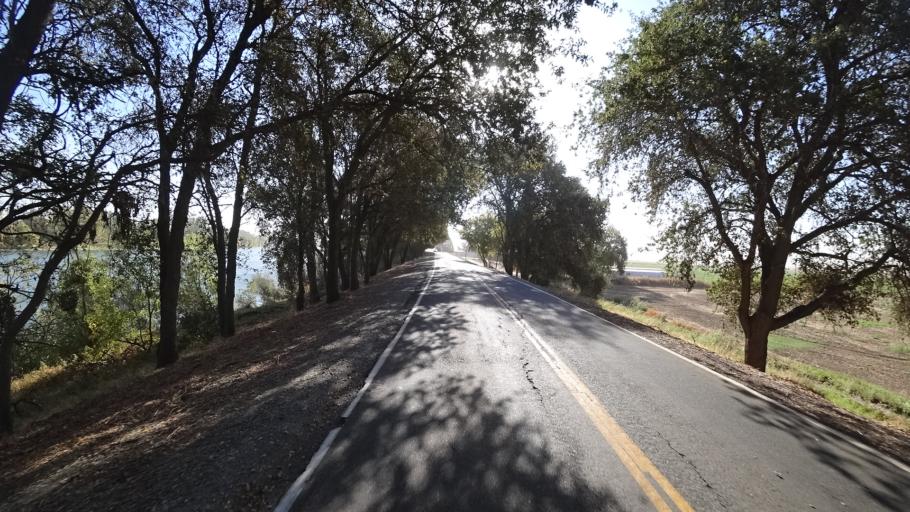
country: US
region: California
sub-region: Sacramento County
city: Parkway
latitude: 38.4760
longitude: -121.5442
